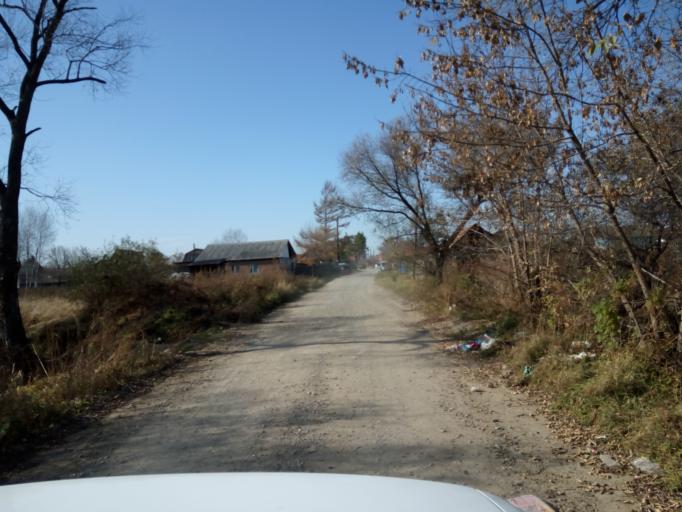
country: RU
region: Primorskiy
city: Dal'nerechensk
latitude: 45.9231
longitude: 133.7238
